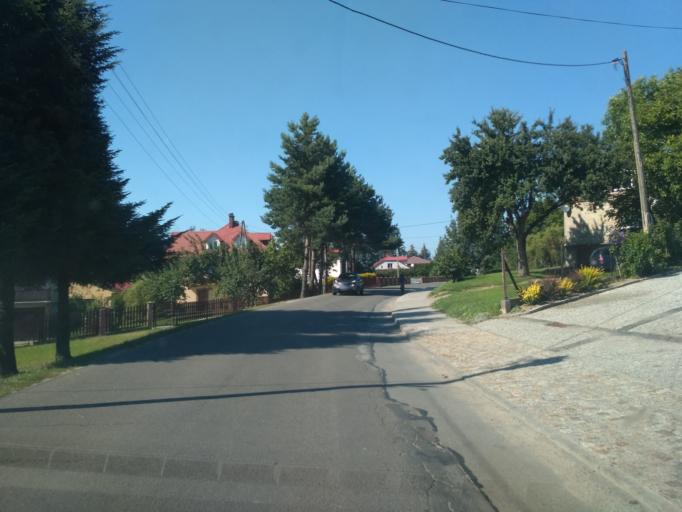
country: PL
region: Subcarpathian Voivodeship
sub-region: Krosno
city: Krosno
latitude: 49.6638
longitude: 21.7523
